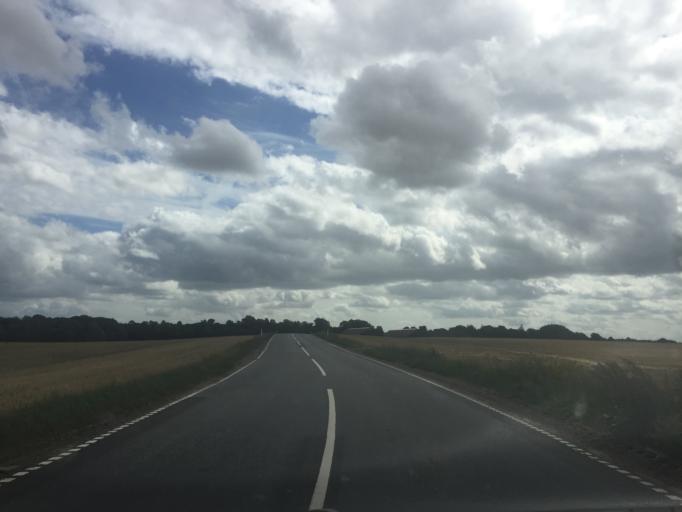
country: DK
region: Capital Region
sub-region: Hoje-Taastrup Kommune
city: Flong
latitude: 55.6954
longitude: 12.2347
